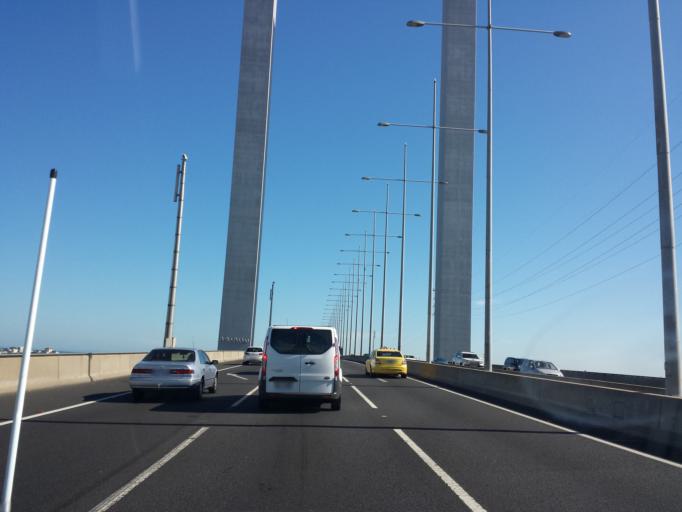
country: AU
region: Victoria
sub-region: Melbourne
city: Docklands
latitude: -37.8183
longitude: 144.9328
